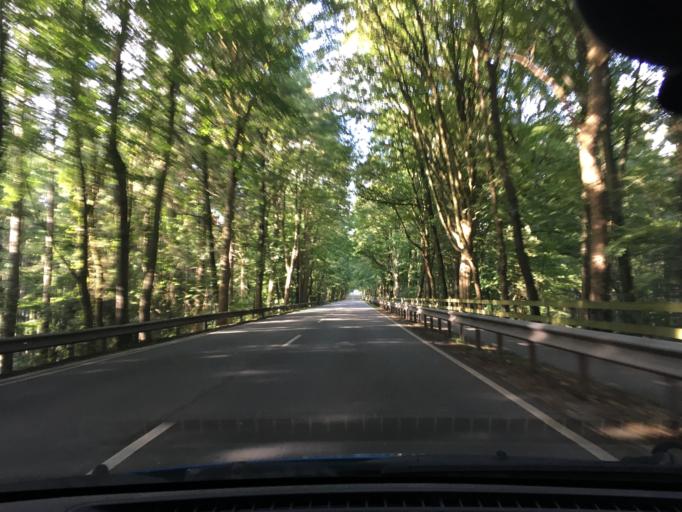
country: DE
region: Lower Saxony
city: Seevetal
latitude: 53.4162
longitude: 9.9282
